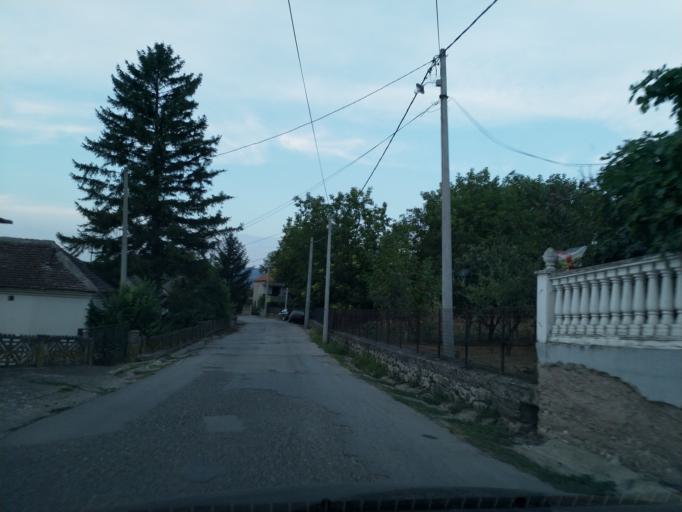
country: RS
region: Central Serbia
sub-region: Pomoravski Okrug
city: Paracin
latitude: 43.8518
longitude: 21.5285
